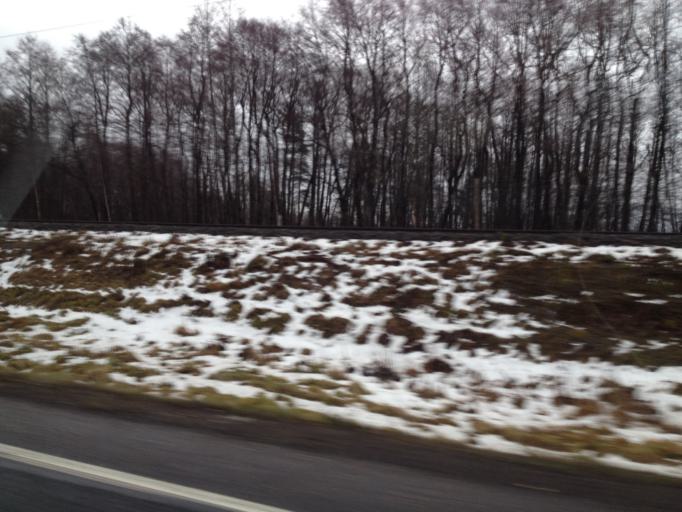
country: FI
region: Uusimaa
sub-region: Raaseporin
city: Ekenaes
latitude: 59.9778
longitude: 23.3993
